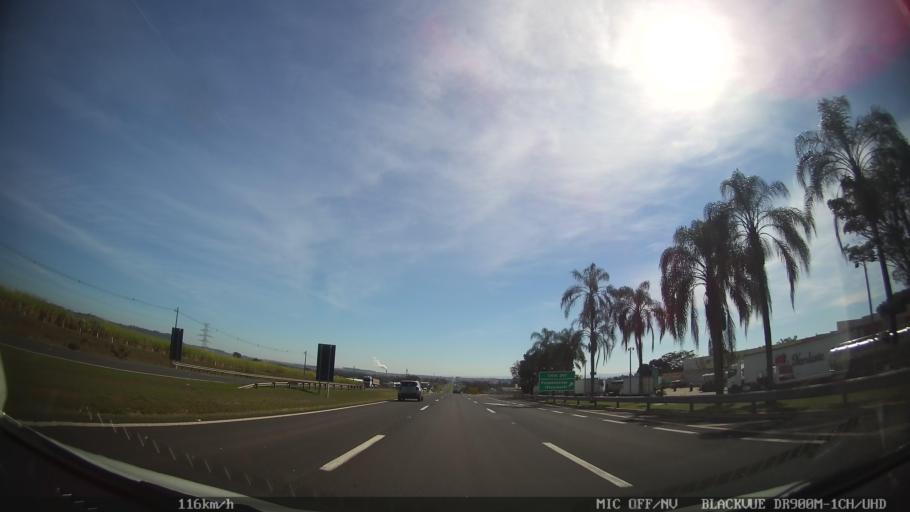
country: BR
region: Sao Paulo
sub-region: Pirassununga
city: Pirassununga
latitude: -22.0320
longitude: -47.4341
